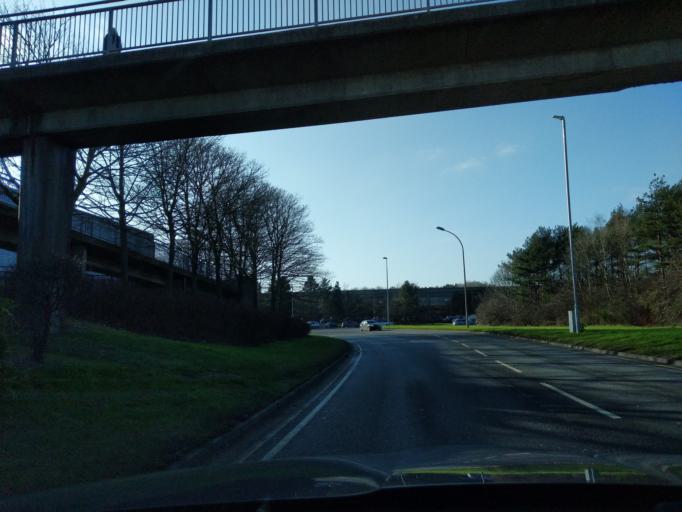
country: GB
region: England
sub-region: Sunderland
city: Washington
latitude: 54.9021
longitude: -1.5332
